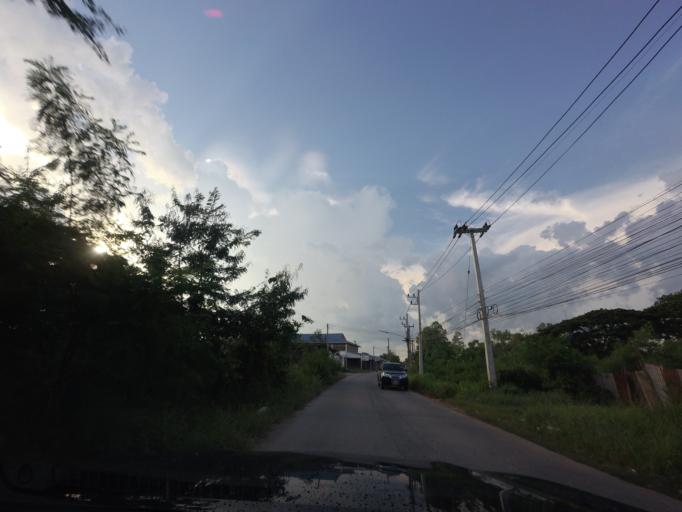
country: TH
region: Khon Kaen
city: Khon Kaen
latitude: 16.4023
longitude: 102.8656
